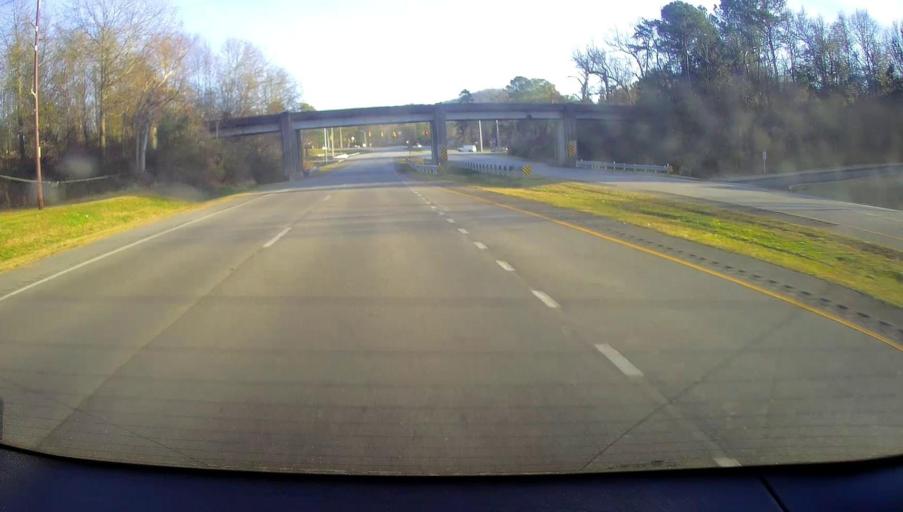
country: US
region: Alabama
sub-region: Calhoun County
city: Saks
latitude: 33.6986
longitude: -85.8267
